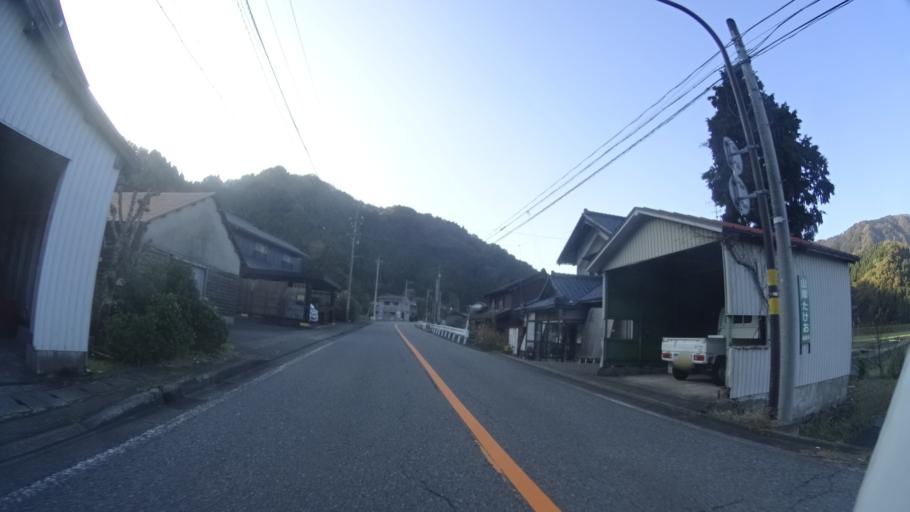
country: JP
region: Fukui
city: Ono
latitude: 35.9952
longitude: 136.4606
